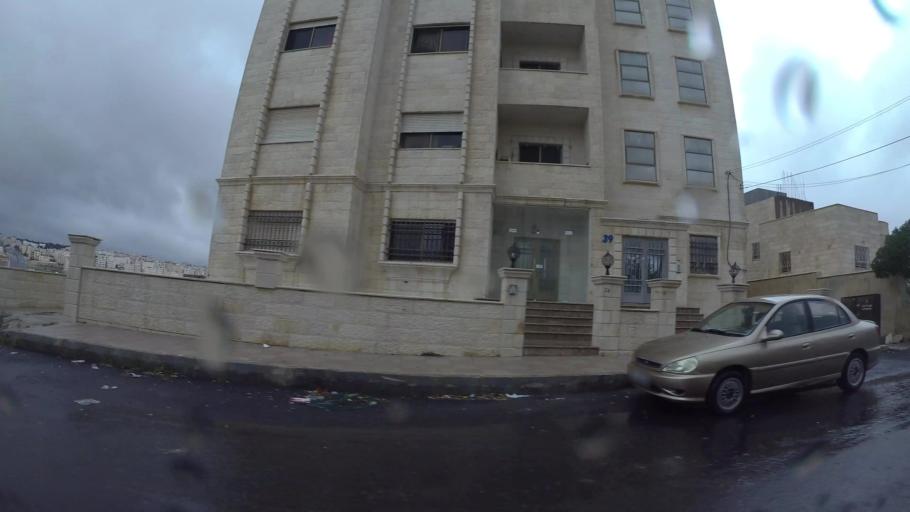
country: JO
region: Amman
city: Al Jubayhah
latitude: 32.0437
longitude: 35.8865
